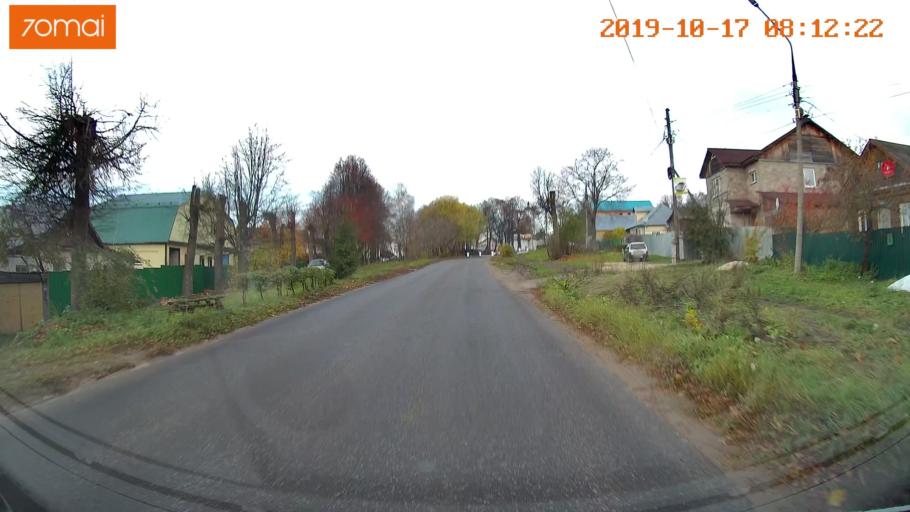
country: RU
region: Vladimir
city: Kol'chugino
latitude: 56.2994
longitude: 39.3593
